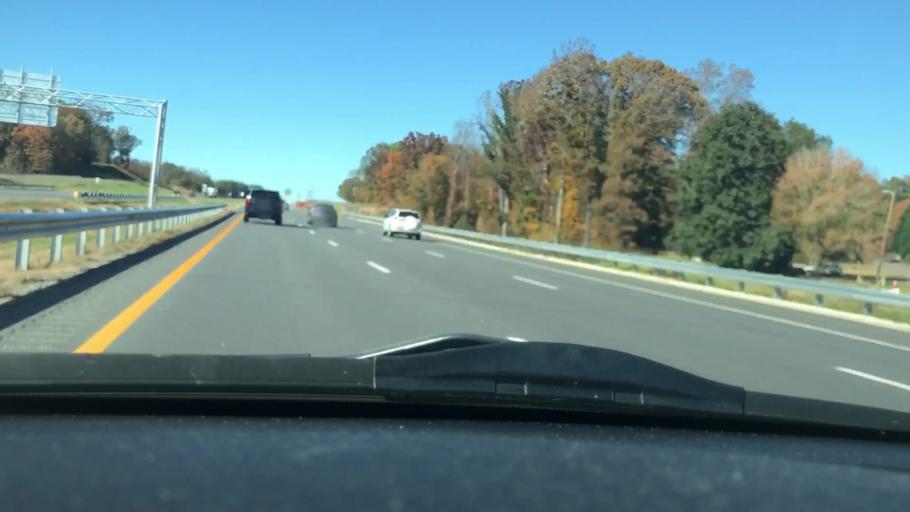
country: US
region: North Carolina
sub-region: Guilford County
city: Summerfield
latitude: 36.2306
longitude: -79.9152
